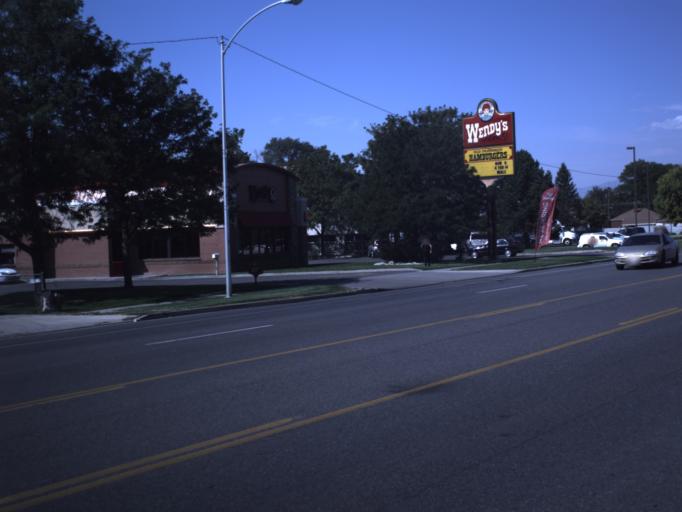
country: US
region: Utah
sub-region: Utah County
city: American Fork
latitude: 40.3747
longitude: -111.7883
